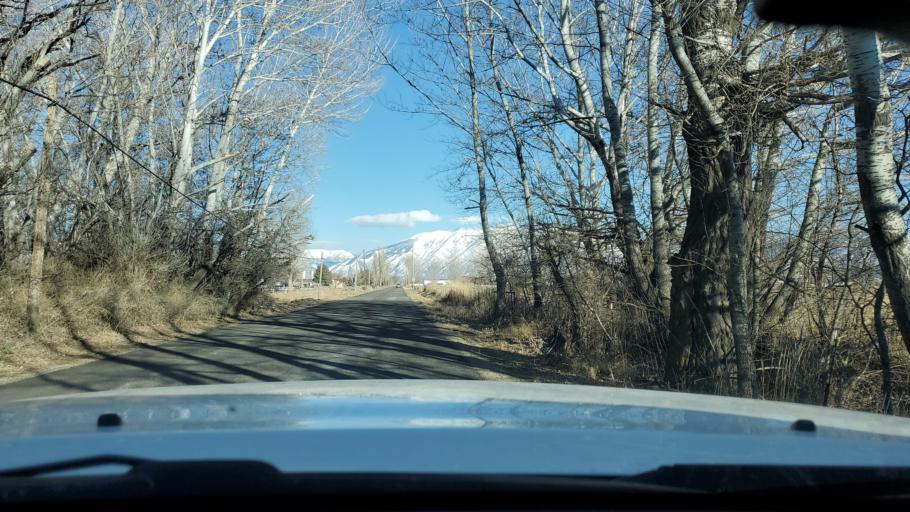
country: US
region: Utah
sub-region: Utah County
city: Benjamin
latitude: 40.1146
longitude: -111.7483
